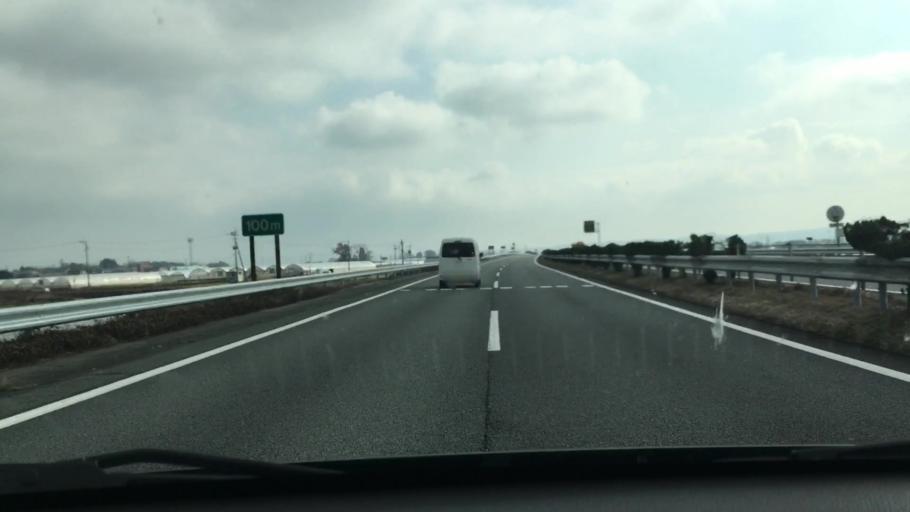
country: JP
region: Kumamoto
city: Ueki
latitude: 32.8843
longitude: 130.7260
